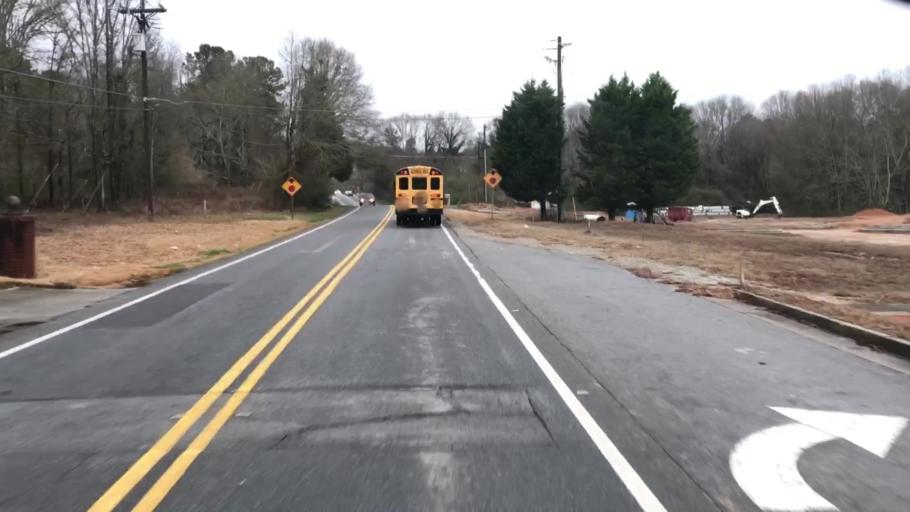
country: US
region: Georgia
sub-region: Walton County
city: Loganville
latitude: 33.8017
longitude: -83.9671
